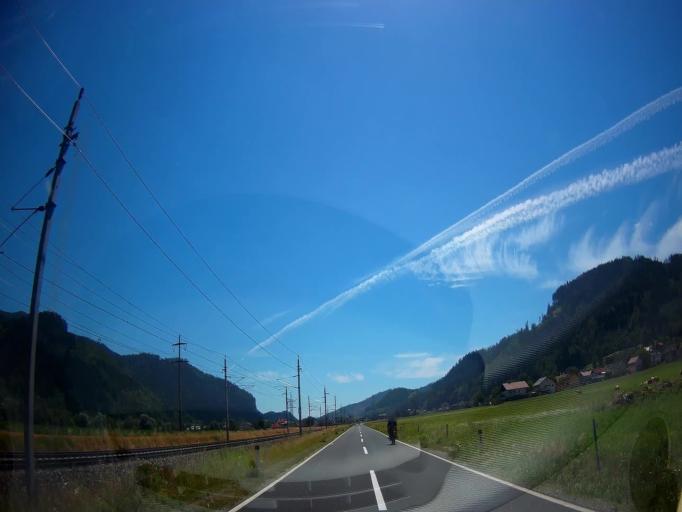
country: AT
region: Carinthia
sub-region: Politischer Bezirk Sankt Veit an der Glan
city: Micheldorf
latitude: 46.9187
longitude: 14.4300
